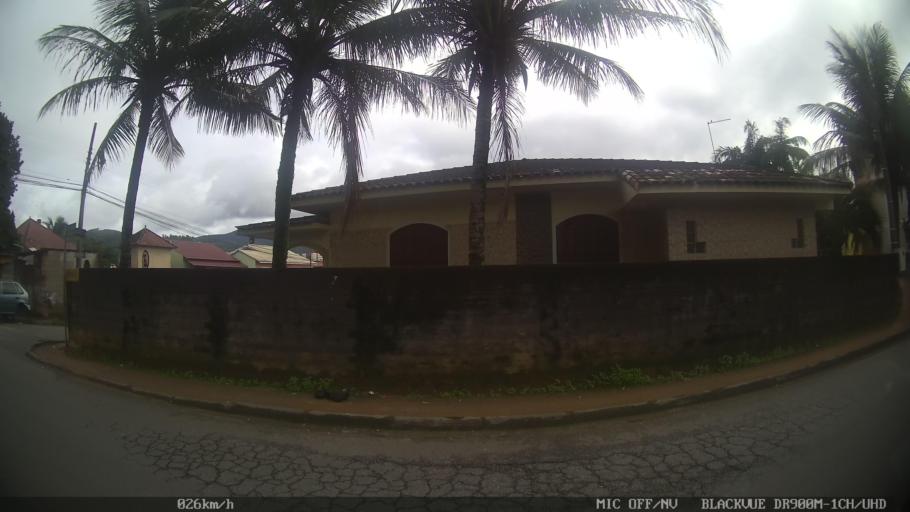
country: BR
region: Santa Catarina
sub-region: Biguacu
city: Biguacu
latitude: -27.5328
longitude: -48.6387
